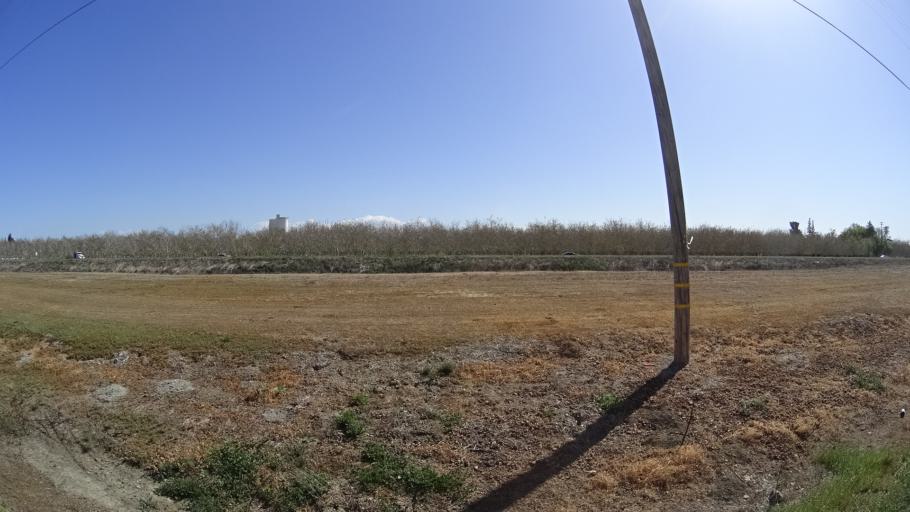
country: US
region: California
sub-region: Glenn County
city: Hamilton City
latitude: 39.7332
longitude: -122.0152
